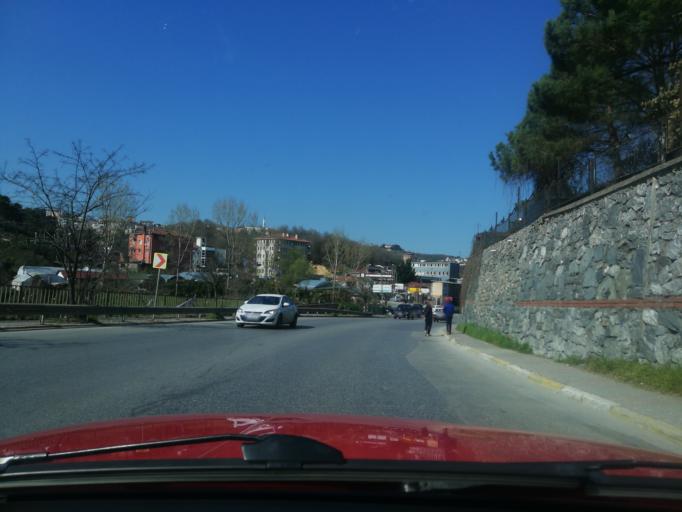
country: TR
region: Istanbul
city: Umraniye
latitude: 41.0847
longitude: 29.1359
